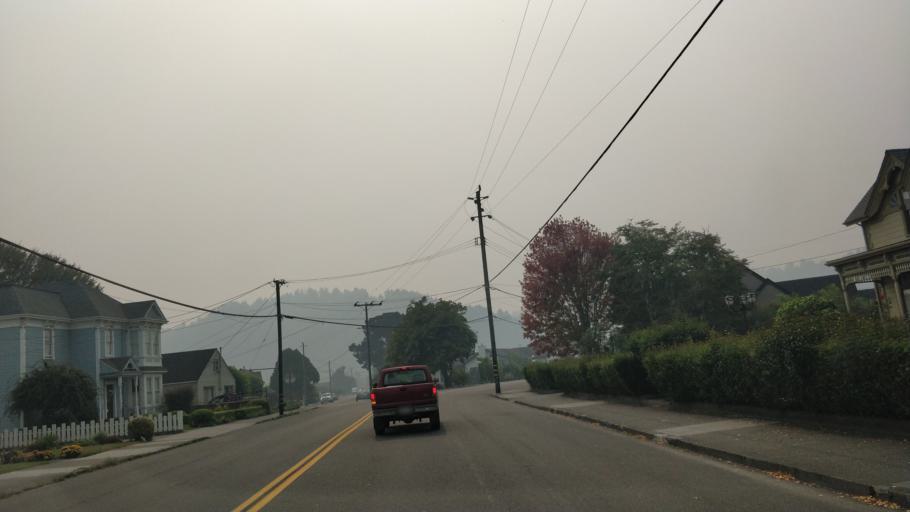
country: US
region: California
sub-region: Humboldt County
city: Ferndale
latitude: 40.5817
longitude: -124.2598
